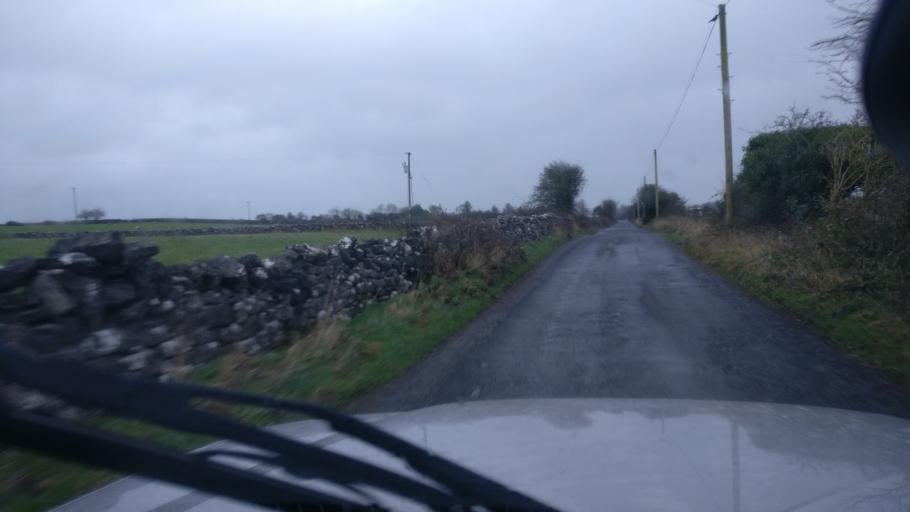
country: IE
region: Connaught
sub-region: County Galway
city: Loughrea
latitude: 53.2310
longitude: -8.6074
